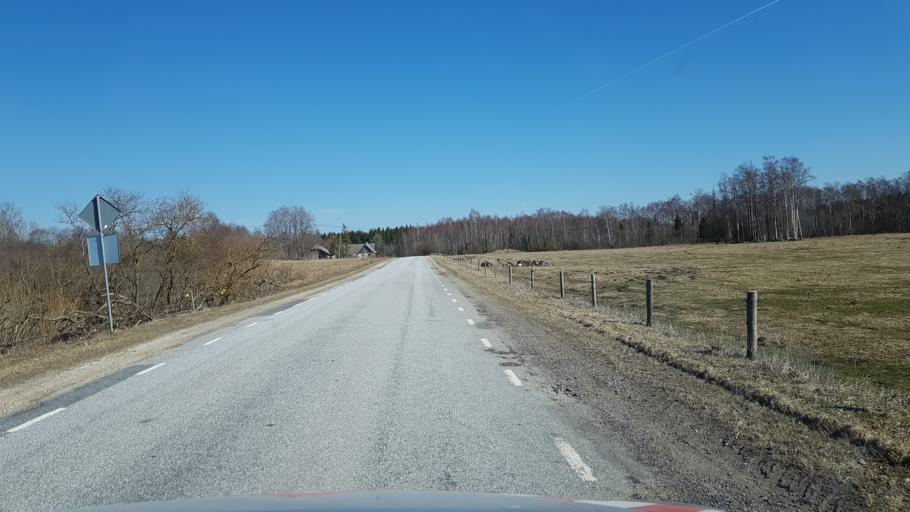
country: EE
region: Jaervamaa
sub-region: Koeru vald
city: Koeru
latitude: 59.0518
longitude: 26.0897
